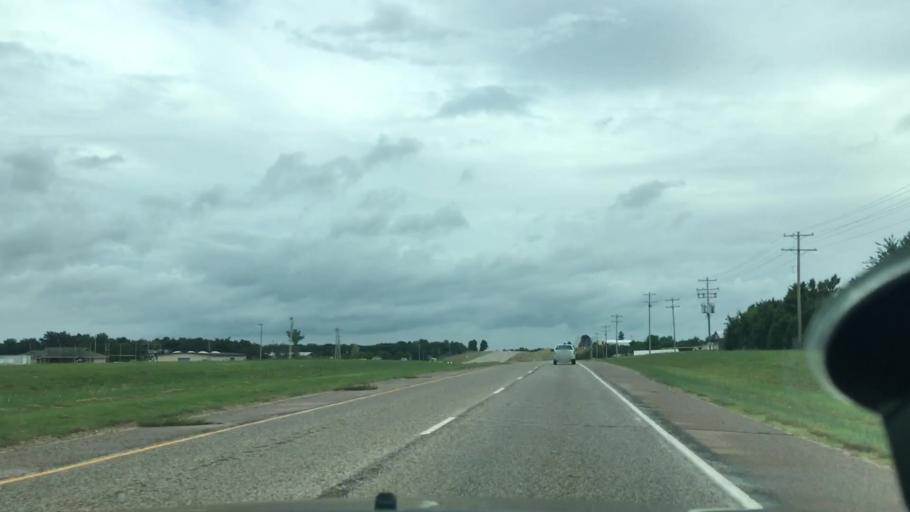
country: US
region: Oklahoma
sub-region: Seminole County
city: Seminole
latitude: 35.2809
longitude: -96.6712
